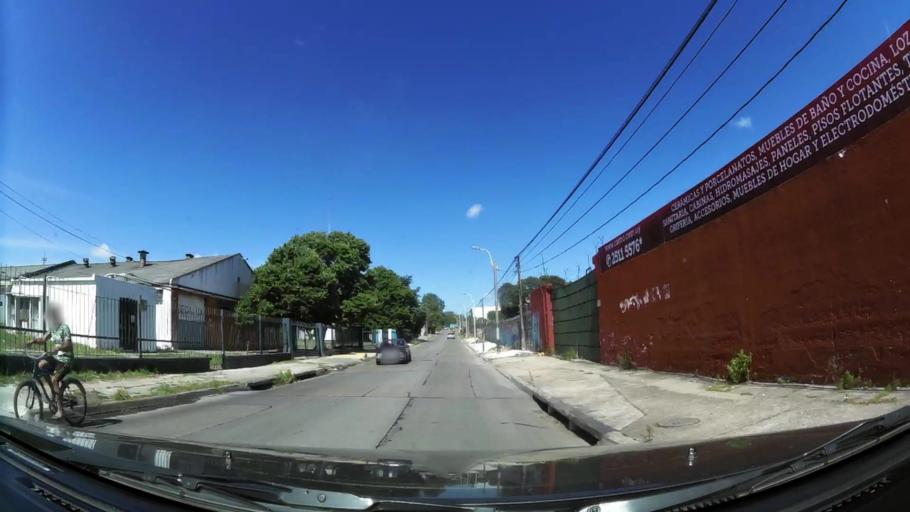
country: UY
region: Canelones
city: Paso de Carrasco
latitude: -34.8462
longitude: -56.1275
